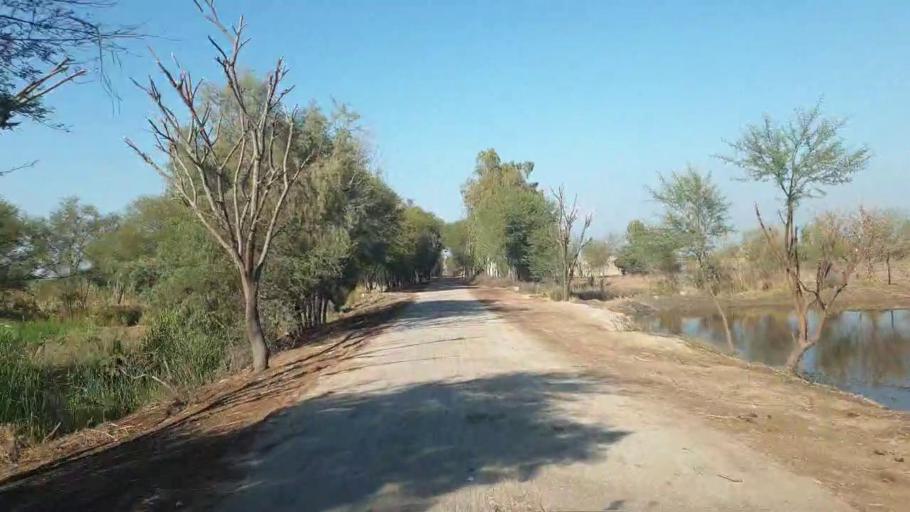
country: PK
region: Sindh
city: Shahdadpur
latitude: 25.9244
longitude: 68.5301
